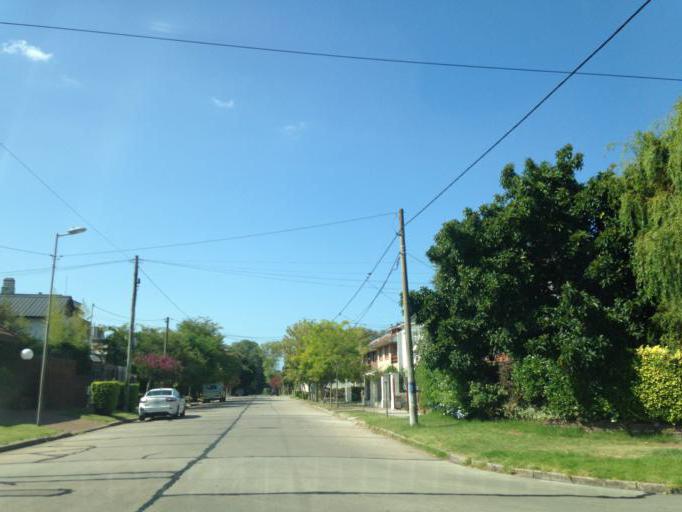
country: AR
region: Buenos Aires
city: Mar del Plata
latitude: -38.0286
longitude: -57.5451
